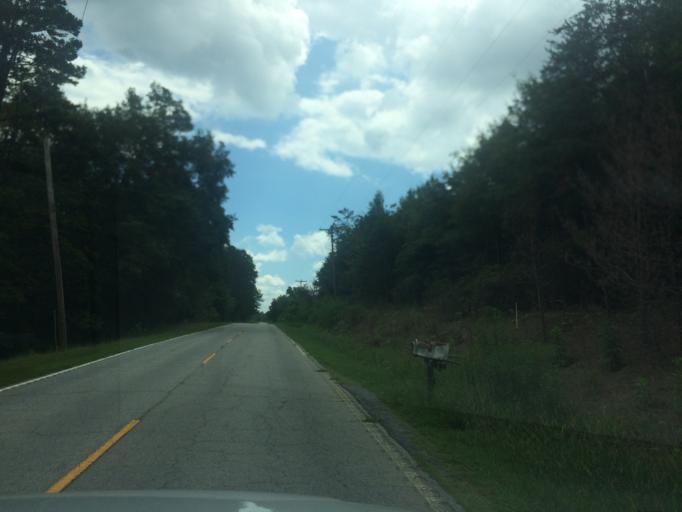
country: US
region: South Carolina
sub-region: Spartanburg County
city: Boiling Springs
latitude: 35.1773
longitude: -82.0342
